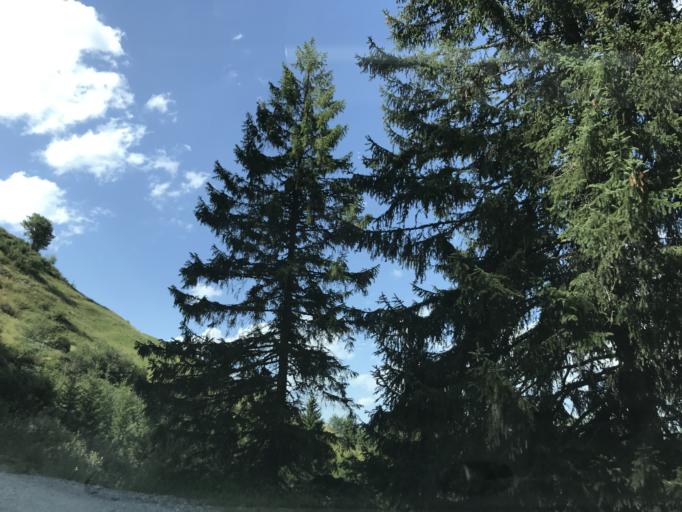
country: FR
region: Rhone-Alpes
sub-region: Departement de la Savoie
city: Beaufort
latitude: 45.6775
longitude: 6.6116
